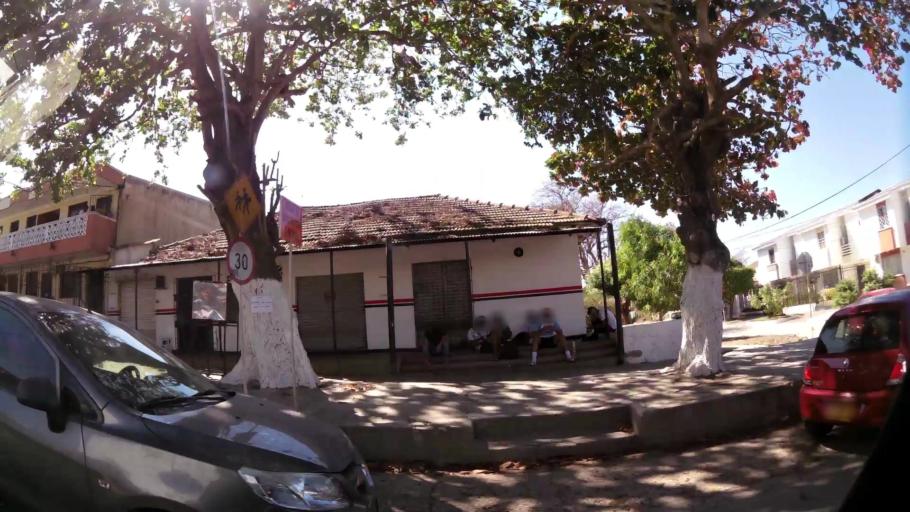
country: CO
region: Atlantico
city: Barranquilla
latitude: 10.9969
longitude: -74.7885
